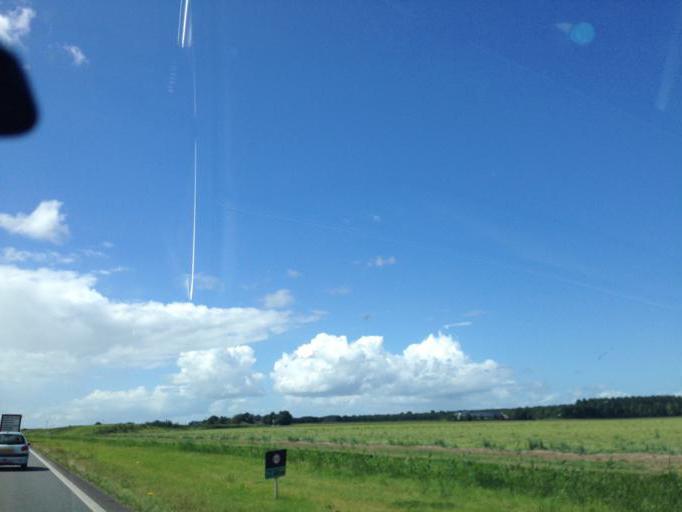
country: NL
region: Flevoland
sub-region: Gemeente Dronten
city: Dronten
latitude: 52.5487
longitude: 5.6525
